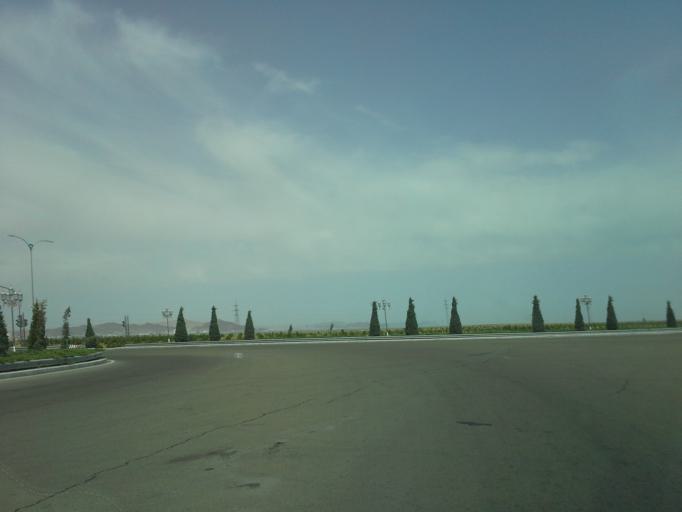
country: TM
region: Balkan
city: Turkmenbasy
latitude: 39.9654
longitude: 52.8642
